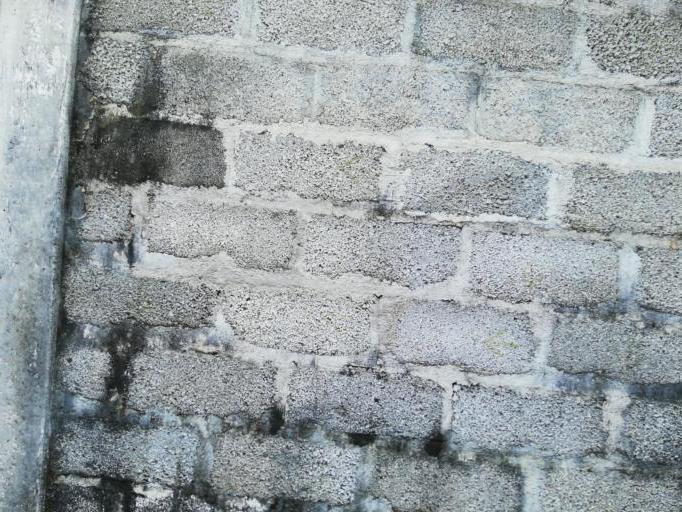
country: MU
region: Moka
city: Moka
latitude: -20.2206
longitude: 57.4760
